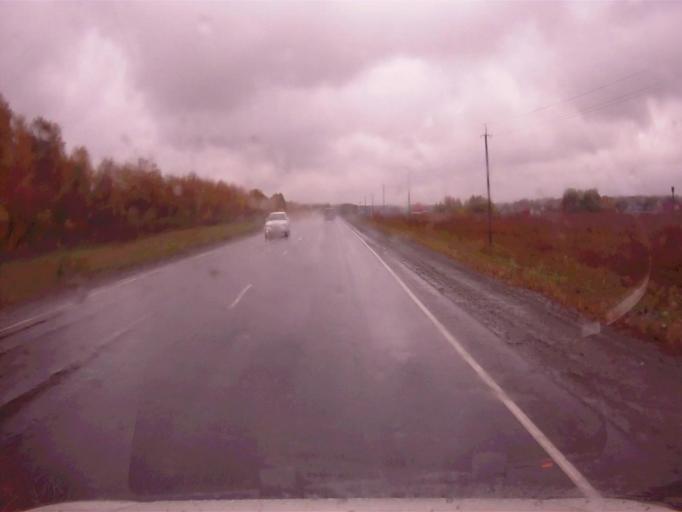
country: RU
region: Chelyabinsk
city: Argayash
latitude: 55.4050
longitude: 61.0621
